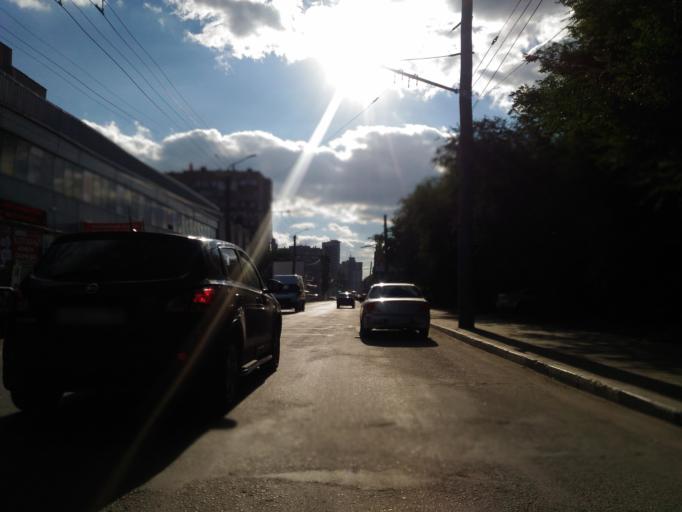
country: RU
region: Voronezj
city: Voronezh
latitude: 51.6517
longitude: 39.1342
